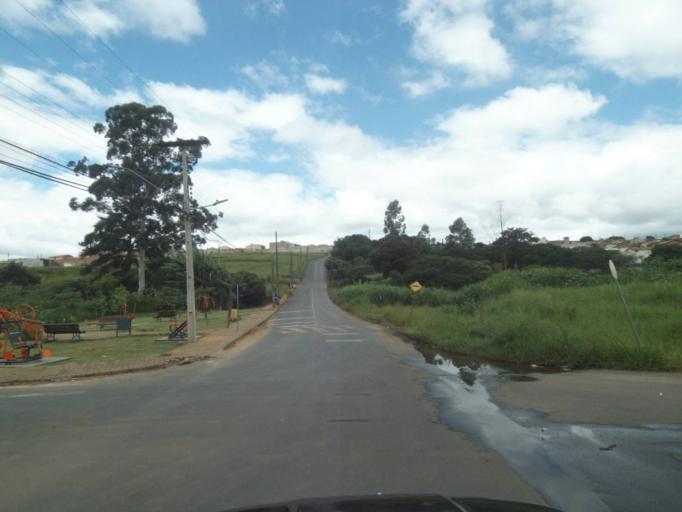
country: BR
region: Parana
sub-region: Telemaco Borba
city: Telemaco Borba
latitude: -24.3168
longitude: -50.6453
